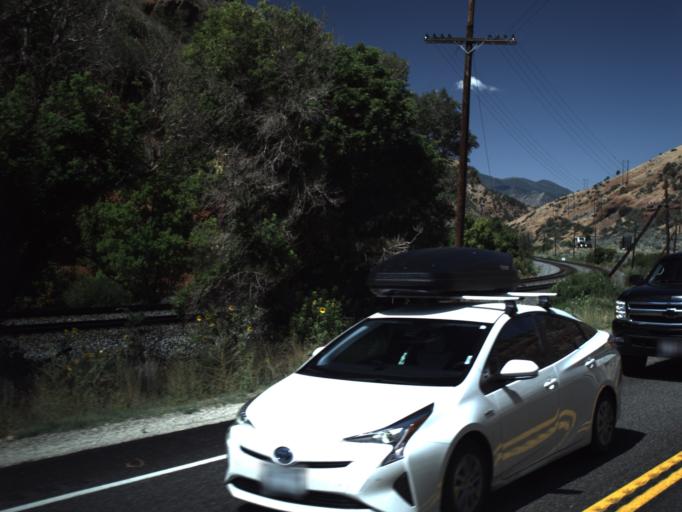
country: US
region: Utah
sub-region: Utah County
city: Mapleton
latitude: 39.9906
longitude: -111.3771
